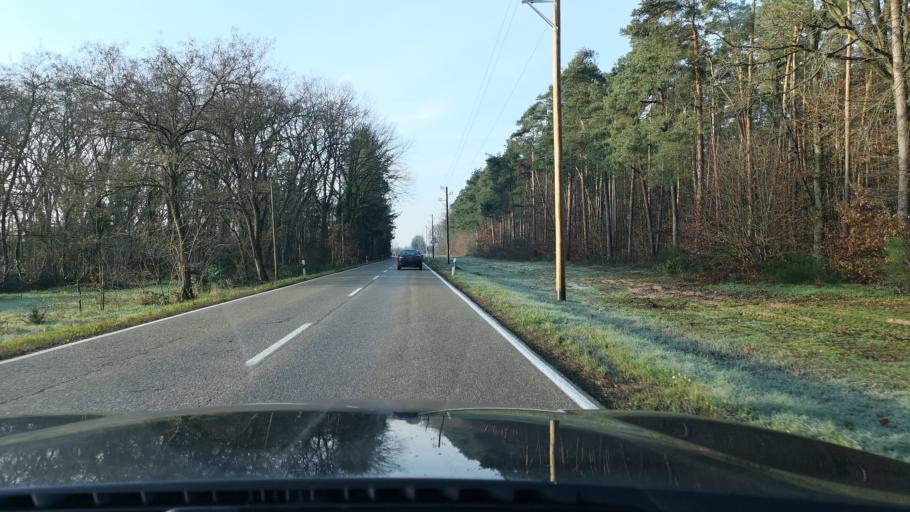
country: DE
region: Rheinland-Pfalz
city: Berg
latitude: 48.9873
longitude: 8.1992
